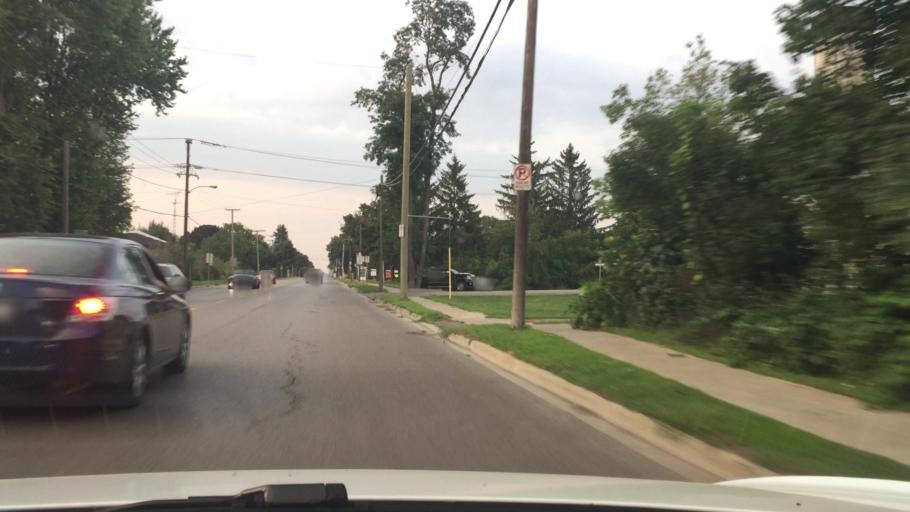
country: CA
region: Ontario
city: Cobourg
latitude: 43.9619
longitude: -78.2911
